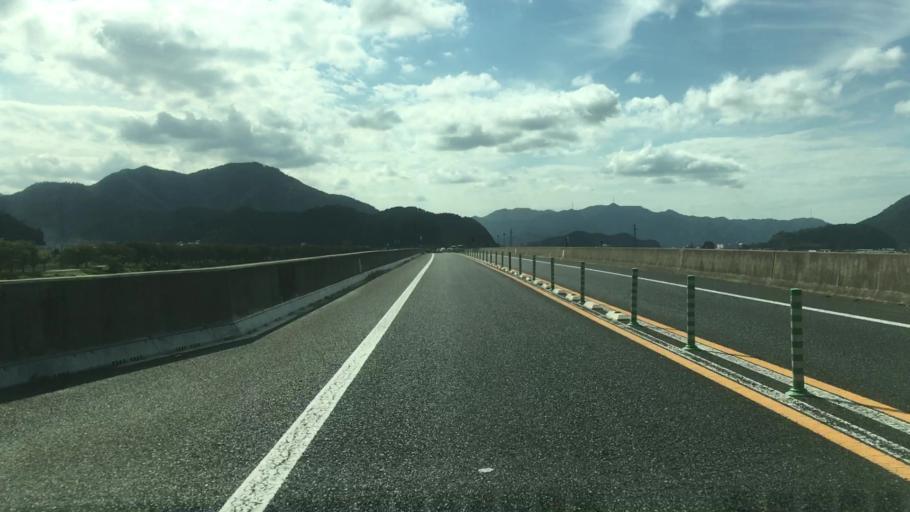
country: JP
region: Kyoto
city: Fukuchiyama
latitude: 35.1998
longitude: 135.0422
